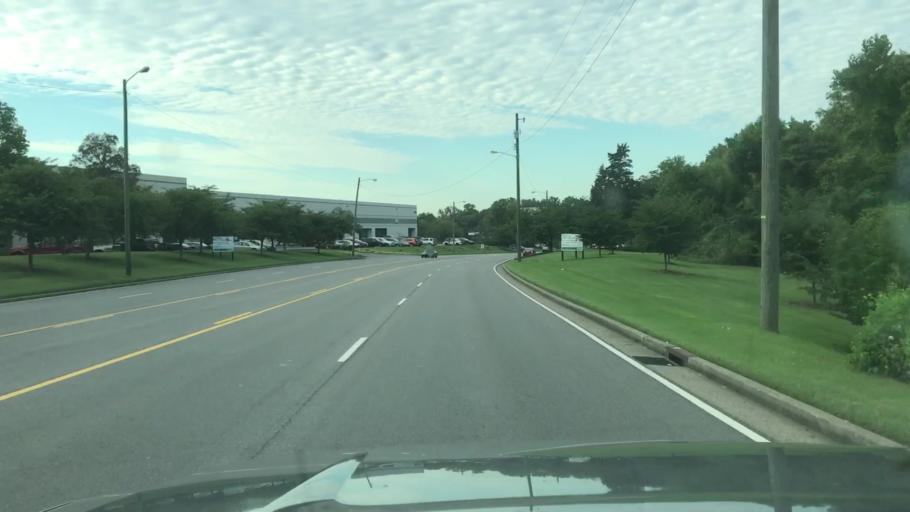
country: US
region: Tennessee
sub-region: Davidson County
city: Oak Hill
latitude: 36.0962
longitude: -86.6777
